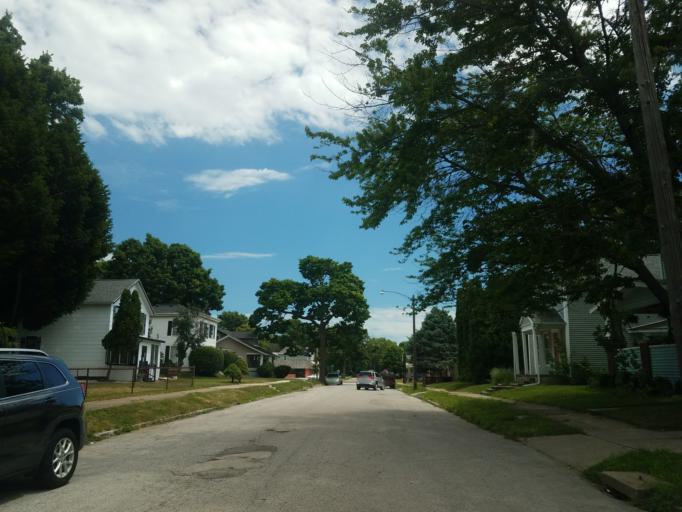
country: US
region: Illinois
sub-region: McLean County
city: Bloomington
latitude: 40.4838
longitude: -88.9861
